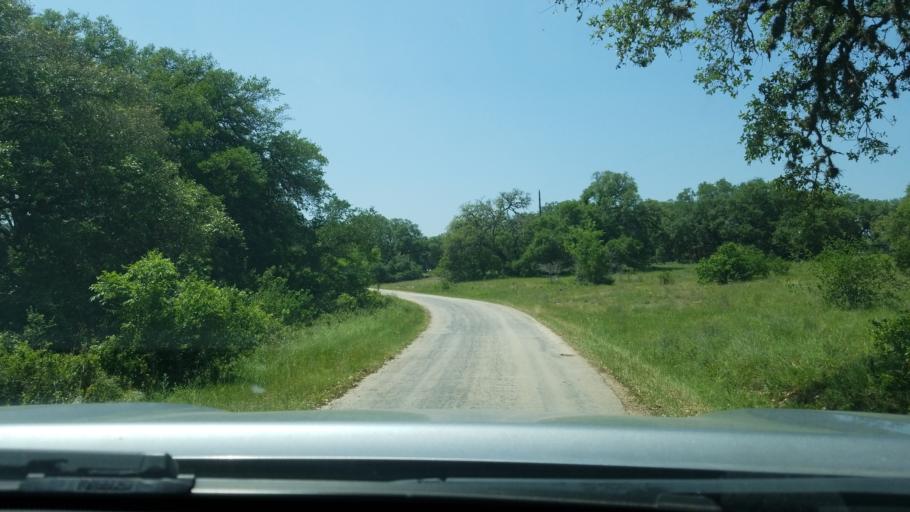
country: US
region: Texas
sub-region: Blanco County
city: Blanco
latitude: 30.0170
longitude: -98.4538
